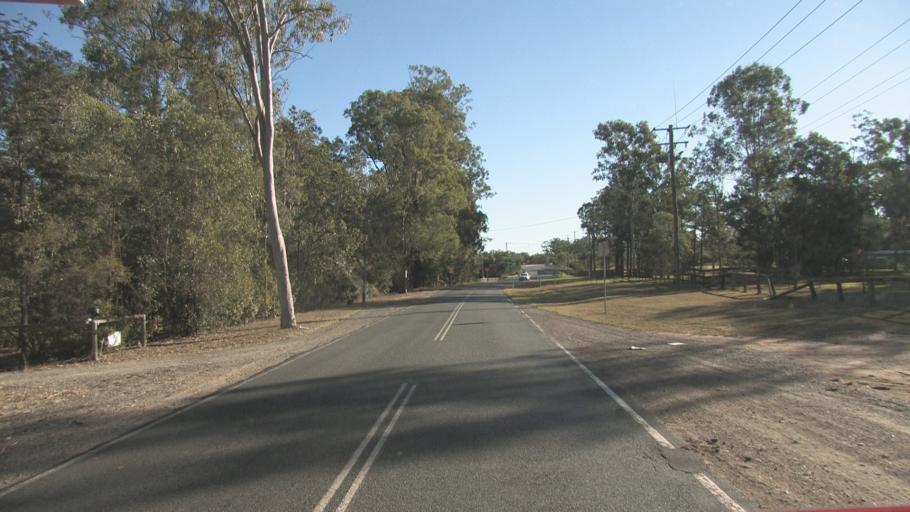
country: AU
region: Queensland
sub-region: Logan
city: North Maclean
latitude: -27.7578
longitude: 153.0278
